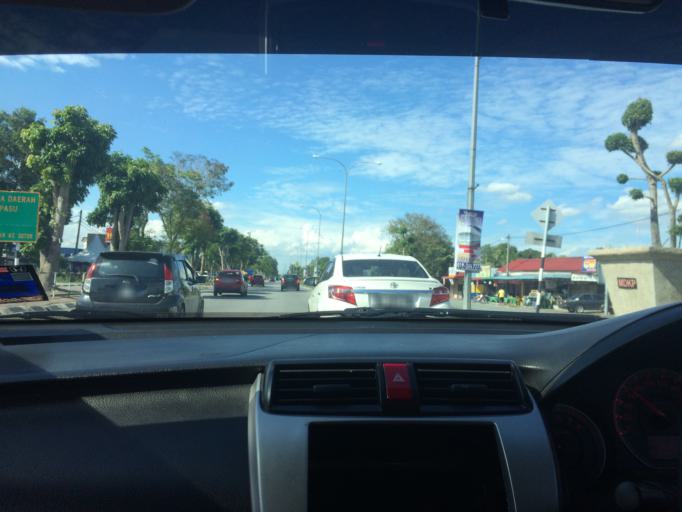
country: MY
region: Kedah
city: Jitra
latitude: 6.2051
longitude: 100.4134
